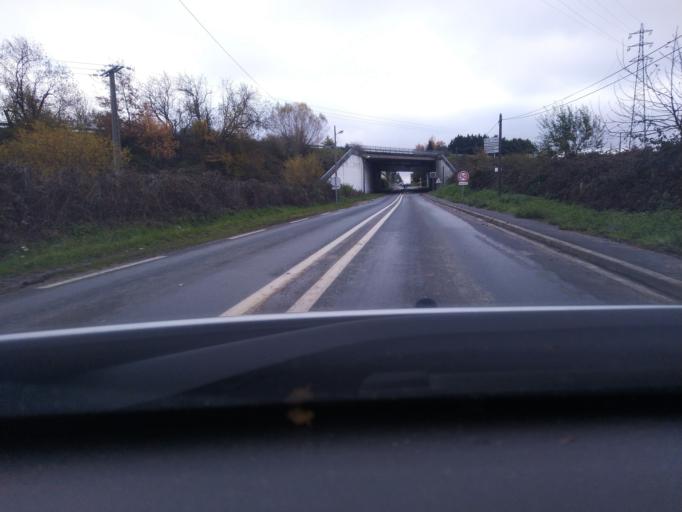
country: FR
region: Haute-Normandie
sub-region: Departement de la Seine-Maritime
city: La Vaupaliere
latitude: 49.4916
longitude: 0.9978
